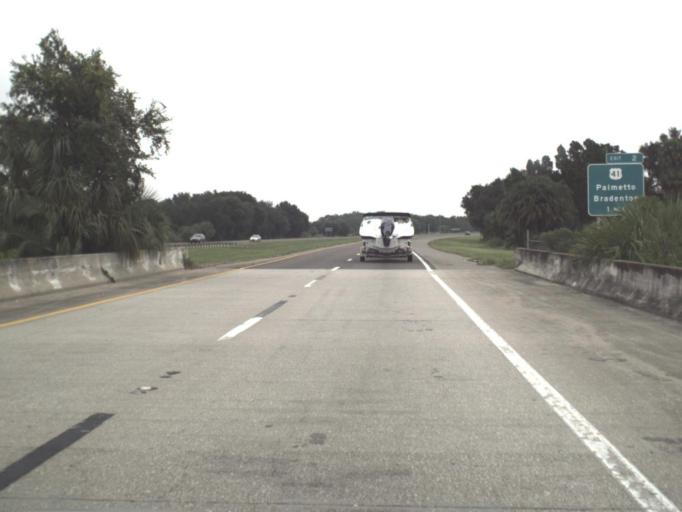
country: US
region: Florida
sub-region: Manatee County
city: Memphis
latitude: 27.5827
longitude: -82.5611
